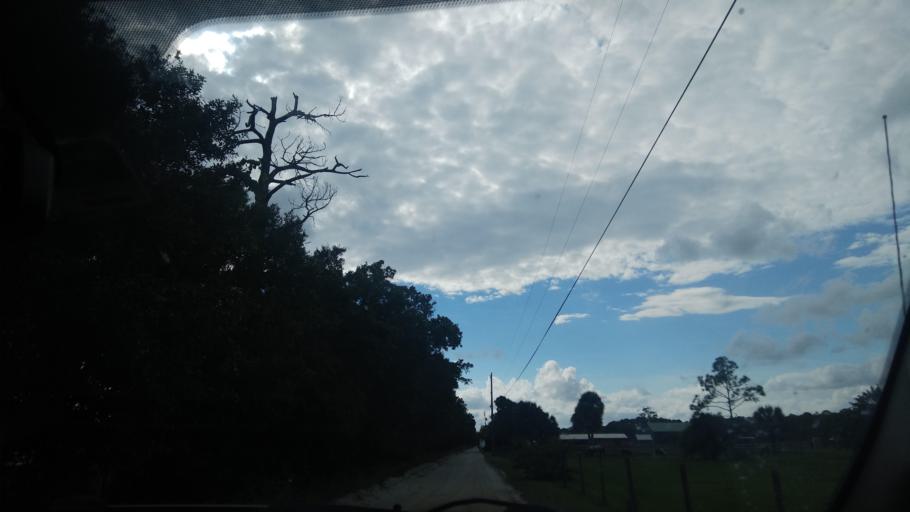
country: US
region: Florida
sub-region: Indian River County
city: Fellsmere
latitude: 27.7864
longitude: -80.5932
